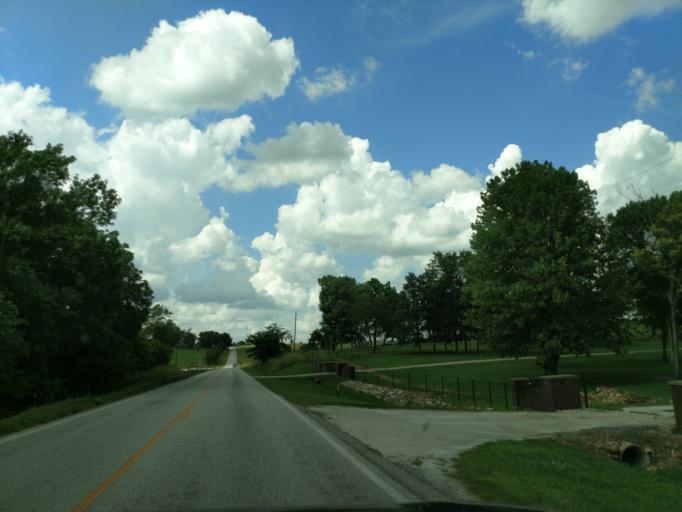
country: US
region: Arkansas
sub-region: Carroll County
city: Berryville
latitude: 36.4240
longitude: -93.5565
